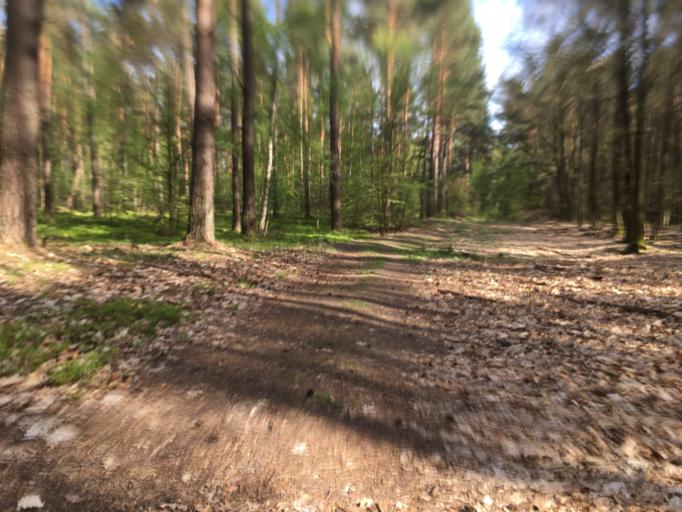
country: DE
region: Brandenburg
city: Bernau bei Berlin
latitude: 52.7147
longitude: 13.5665
